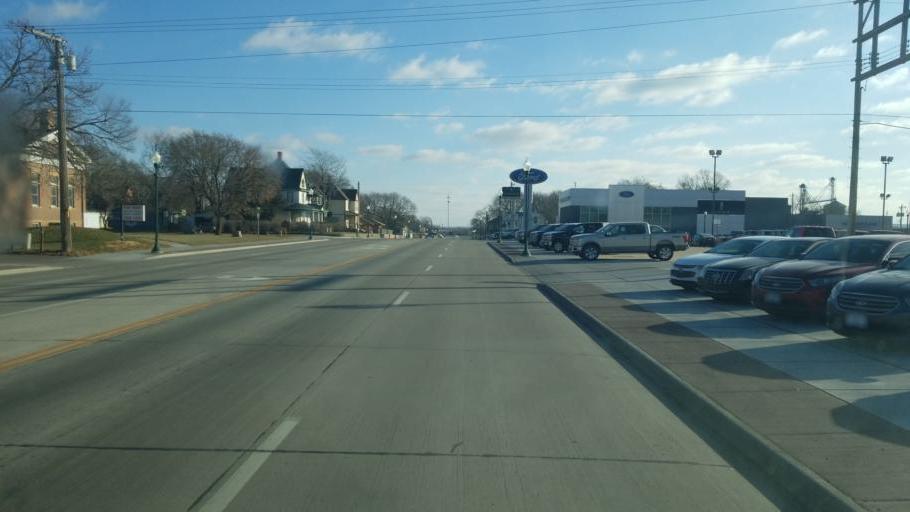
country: US
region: South Dakota
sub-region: Yankton County
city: Yankton
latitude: 42.8711
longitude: -97.3917
